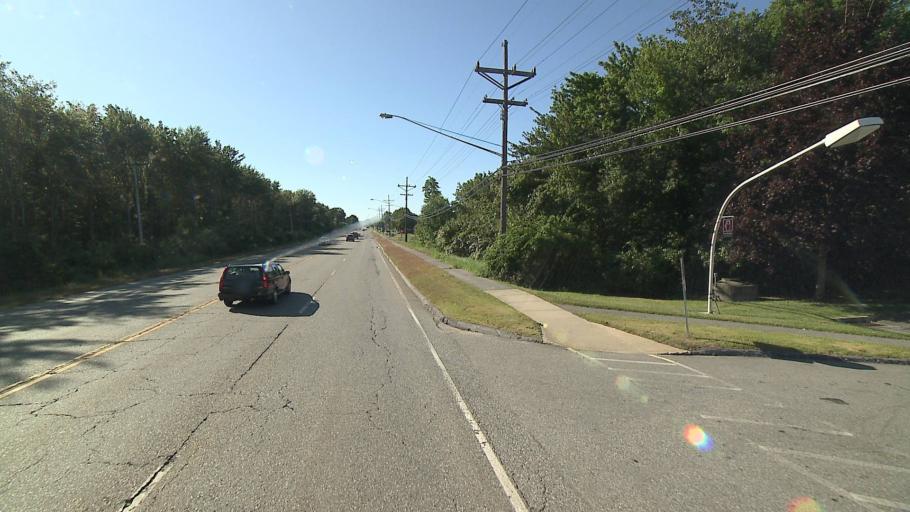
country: US
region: Connecticut
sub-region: New London County
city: Conning Towers-Nautilus Park
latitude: 41.3792
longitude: -72.0758
